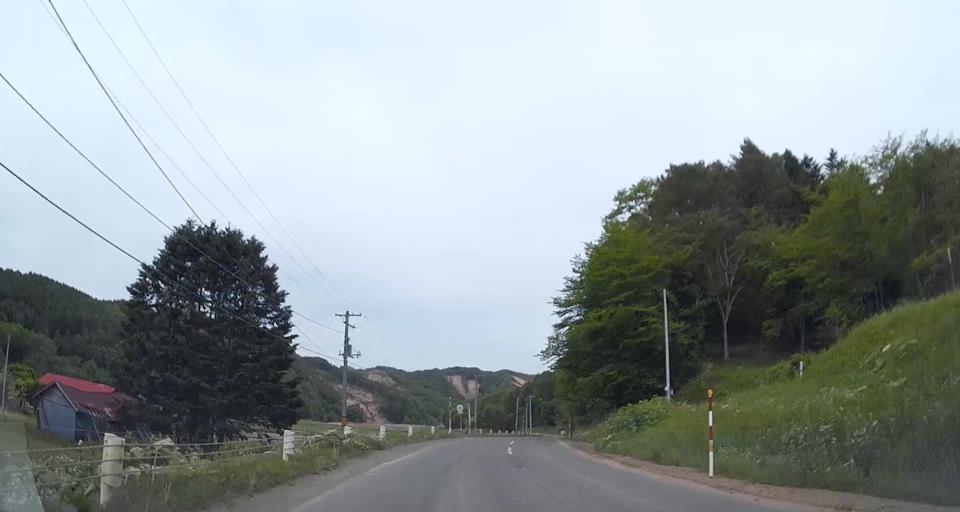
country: JP
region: Hokkaido
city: Chitose
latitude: 42.7563
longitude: 141.9782
